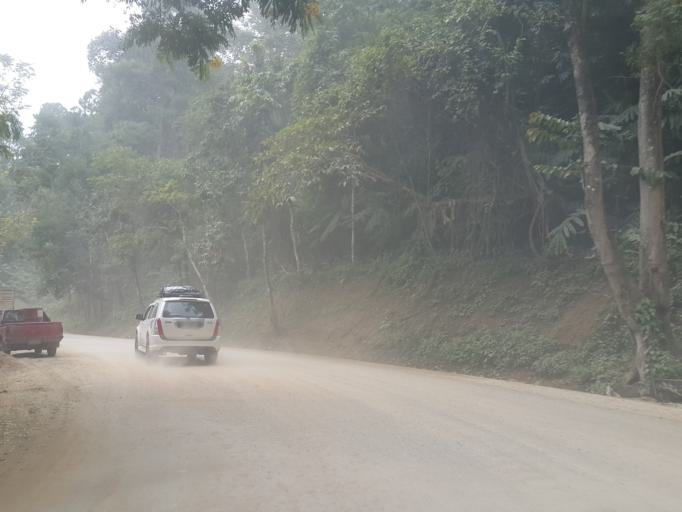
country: TH
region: Mae Hong Son
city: Mae Hi
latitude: 19.2321
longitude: 98.6628
